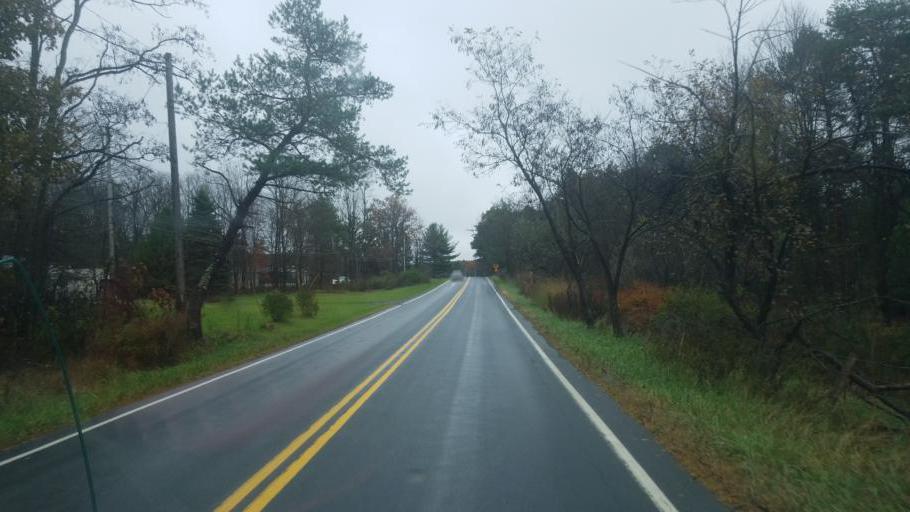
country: US
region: Pennsylvania
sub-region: Centre County
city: Milesburg
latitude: 41.0293
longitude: -77.9755
